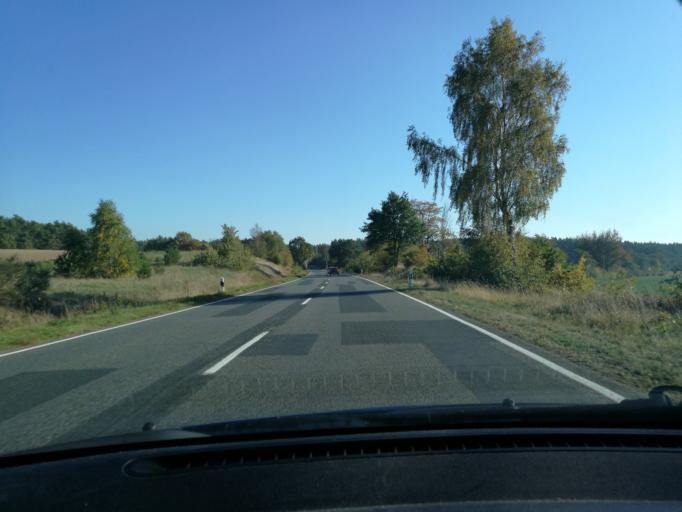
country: DE
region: Lower Saxony
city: Dahlem
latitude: 53.1756
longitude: 10.7697
